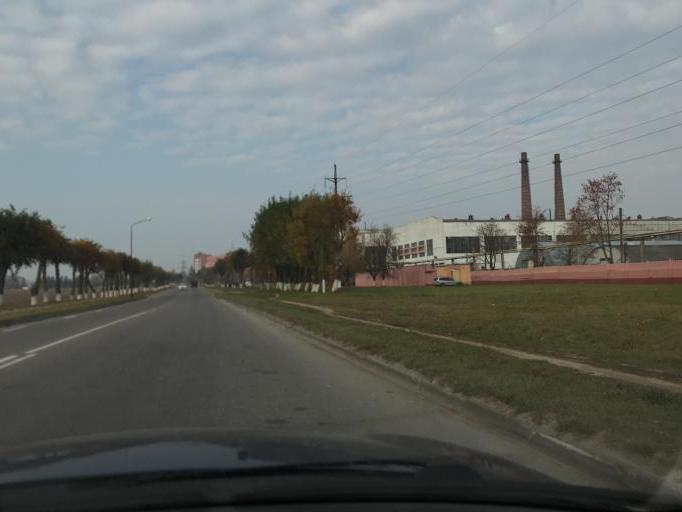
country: BY
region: Grodnenskaya
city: Lida
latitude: 53.8707
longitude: 25.2769
